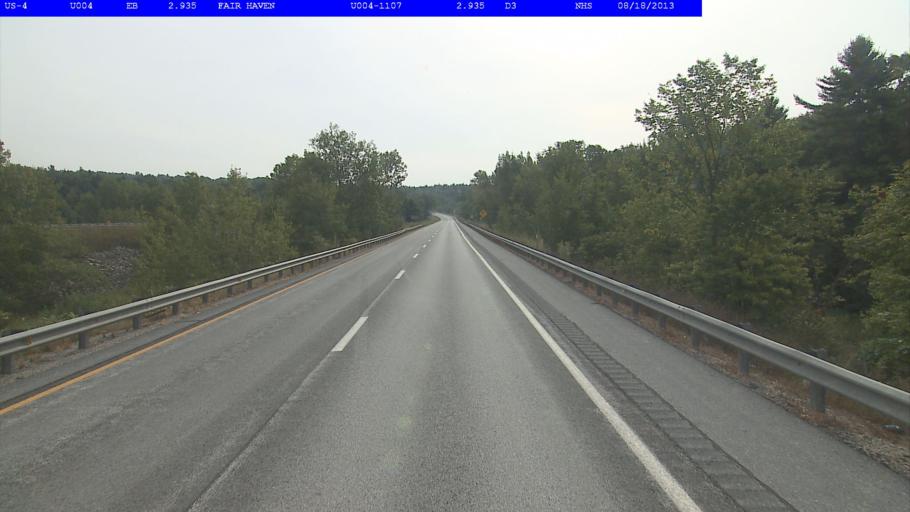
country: US
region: Vermont
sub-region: Rutland County
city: Fair Haven
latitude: 43.6048
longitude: -73.2529
